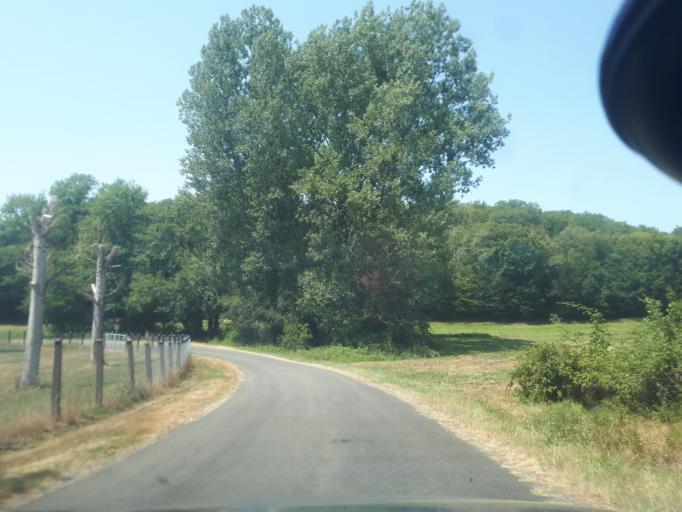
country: FR
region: Midi-Pyrenees
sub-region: Departement du Lot
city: Salviac
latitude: 44.7352
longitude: 1.2744
